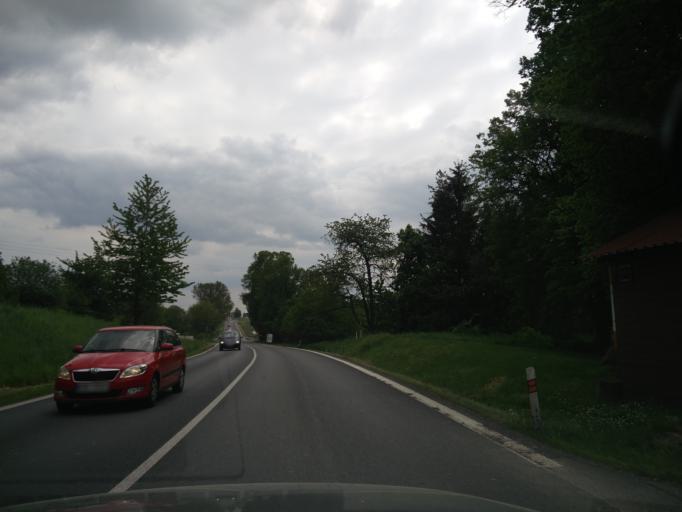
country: CZ
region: Central Bohemia
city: Milin
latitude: 49.5834
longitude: 14.0714
